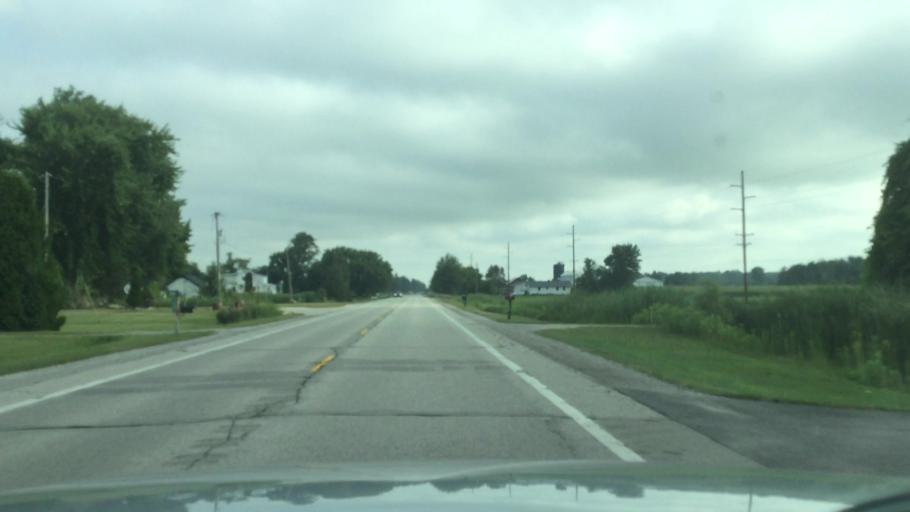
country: US
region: Michigan
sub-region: Saginaw County
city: Birch Run
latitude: 43.2688
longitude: -83.7357
